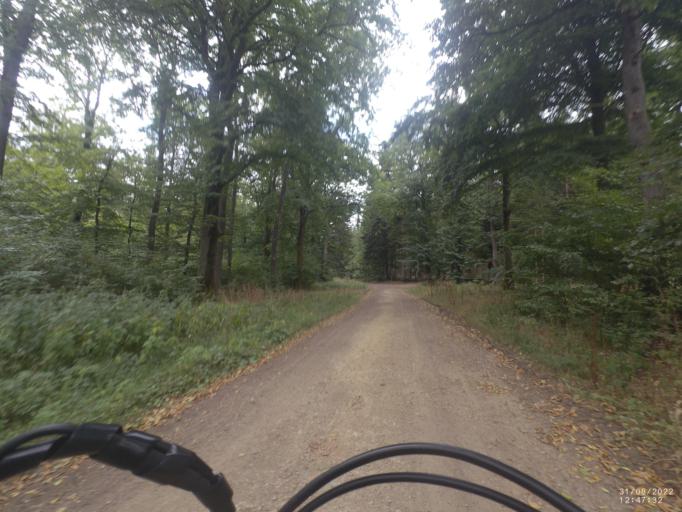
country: DE
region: Rheinland-Pfalz
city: Steffeln
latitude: 50.3106
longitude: 6.5590
